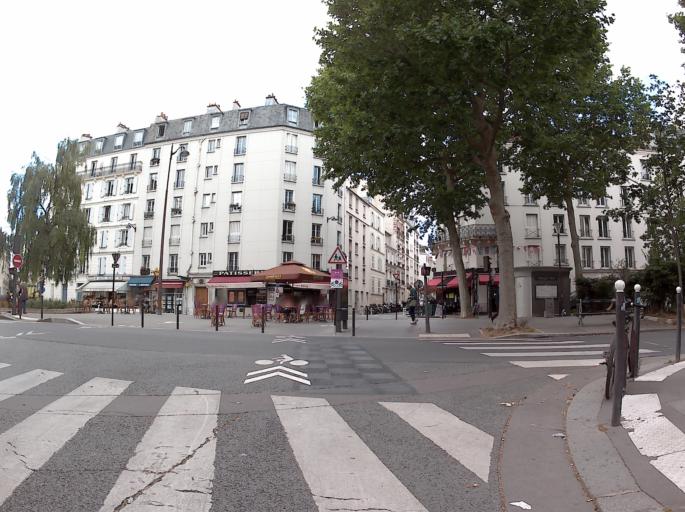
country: FR
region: Ile-de-France
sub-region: Departement du Val-de-Marne
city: Gentilly
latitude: 48.8305
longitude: 2.3343
